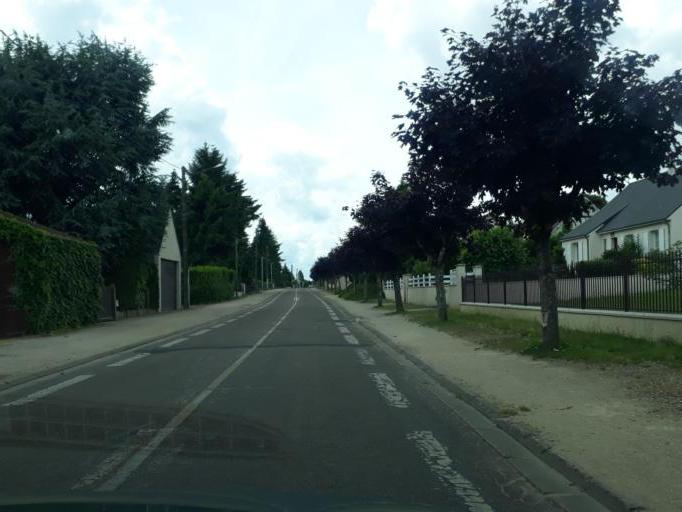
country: FR
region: Centre
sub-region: Departement du Loiret
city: Meung-sur-Loire
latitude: 47.8340
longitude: 1.7094
